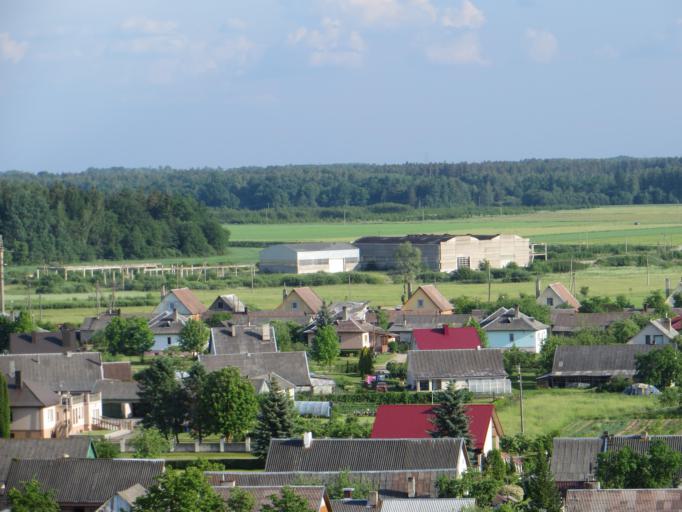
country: LT
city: Kaisiadorys
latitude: 55.0838
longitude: 24.5413
